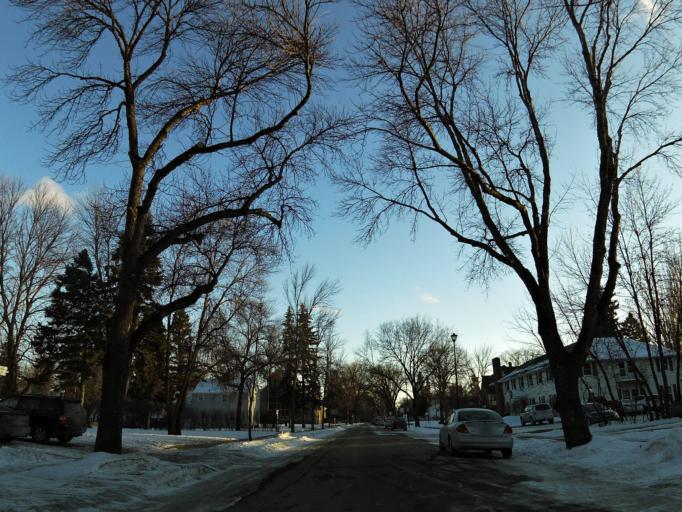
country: US
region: North Dakota
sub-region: Grand Forks County
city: Grand Forks
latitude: 47.9253
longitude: -97.0706
